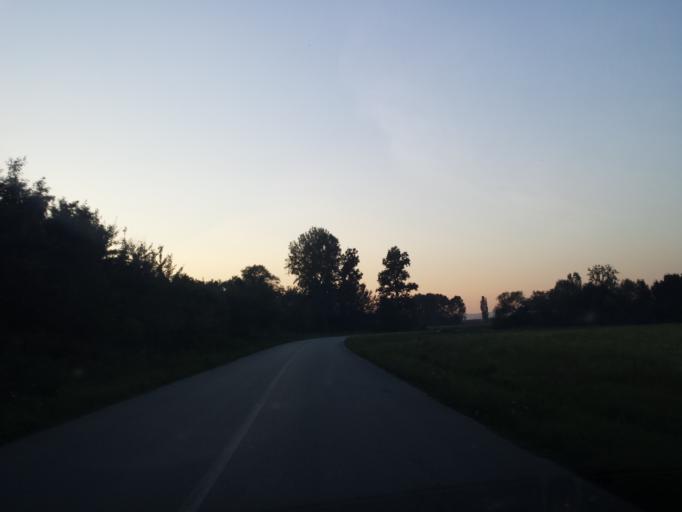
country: HR
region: Brodsko-Posavska
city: Oriovac
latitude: 45.1155
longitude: 17.8227
